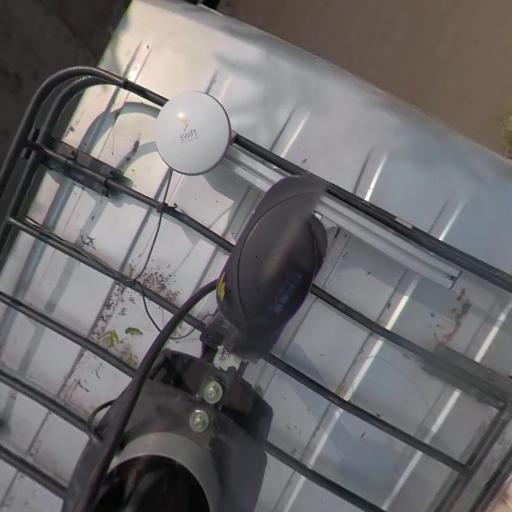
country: IN
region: Telangana
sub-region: Nalgonda
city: Suriapet
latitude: 17.2034
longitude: 79.4843
